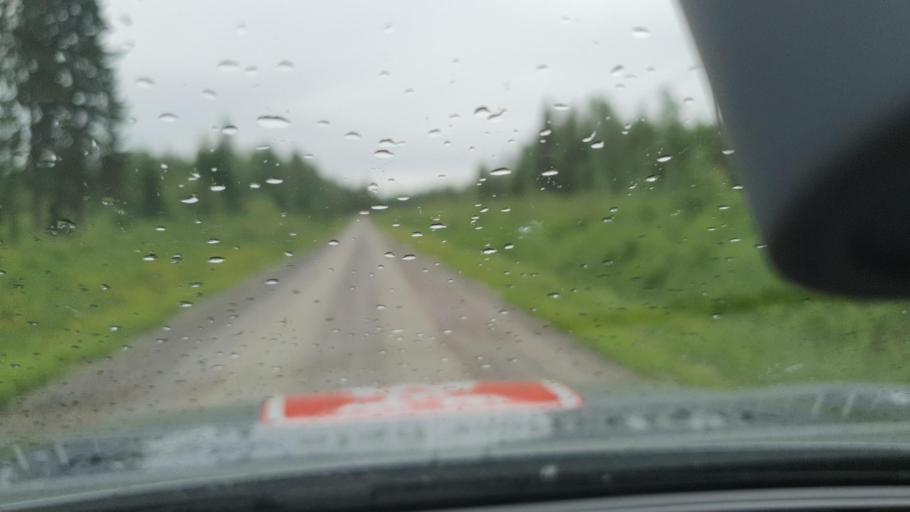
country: SE
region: Norrbotten
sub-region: Kalix Kommun
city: Rolfs
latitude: 66.0686
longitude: 22.9861
